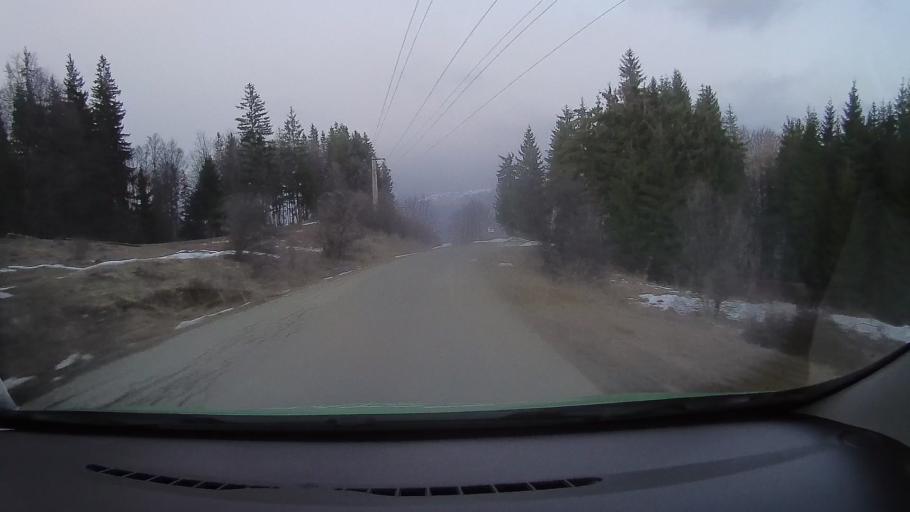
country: RO
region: Prahova
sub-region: Comuna Secaria
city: Secaria
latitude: 45.2905
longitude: 25.7040
